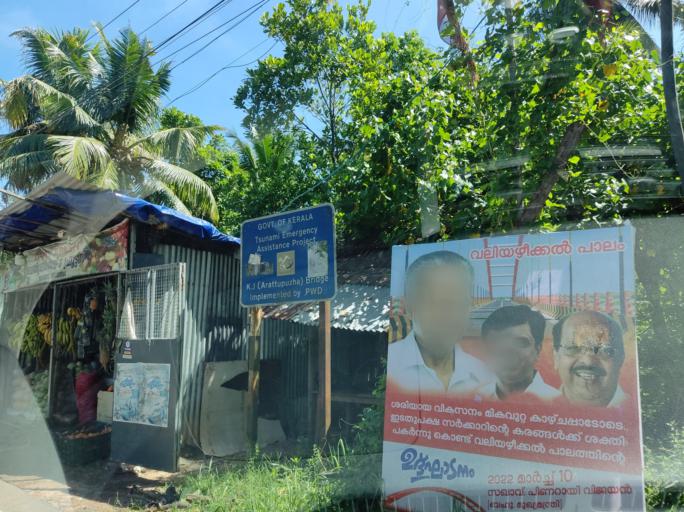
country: IN
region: Kerala
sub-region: Alappuzha
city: Kayankulam
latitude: 9.1714
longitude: 76.4589
